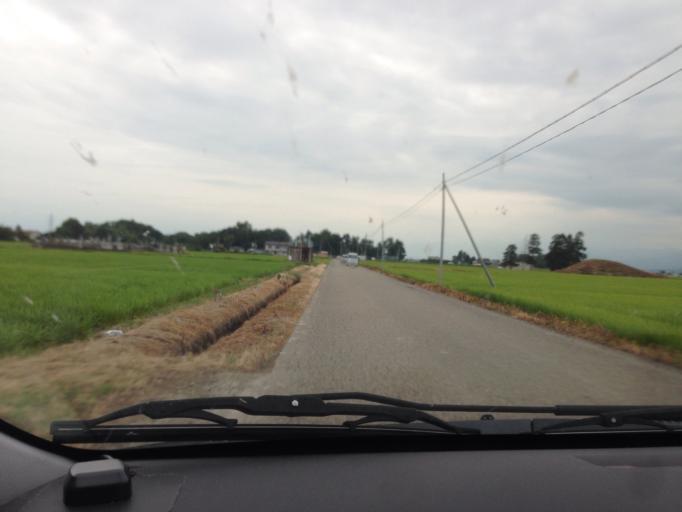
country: JP
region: Fukushima
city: Kitakata
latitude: 37.5063
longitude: 139.8949
